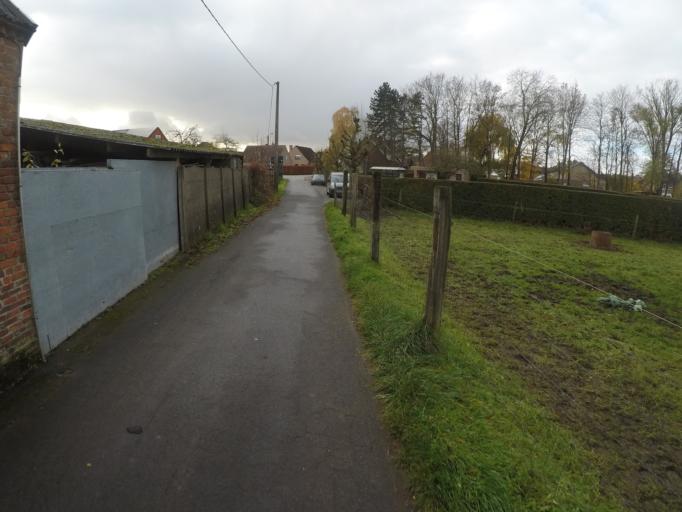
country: BE
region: Flanders
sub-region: Provincie Vlaams-Brabant
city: Opwijk
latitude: 50.9454
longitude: 4.1734
